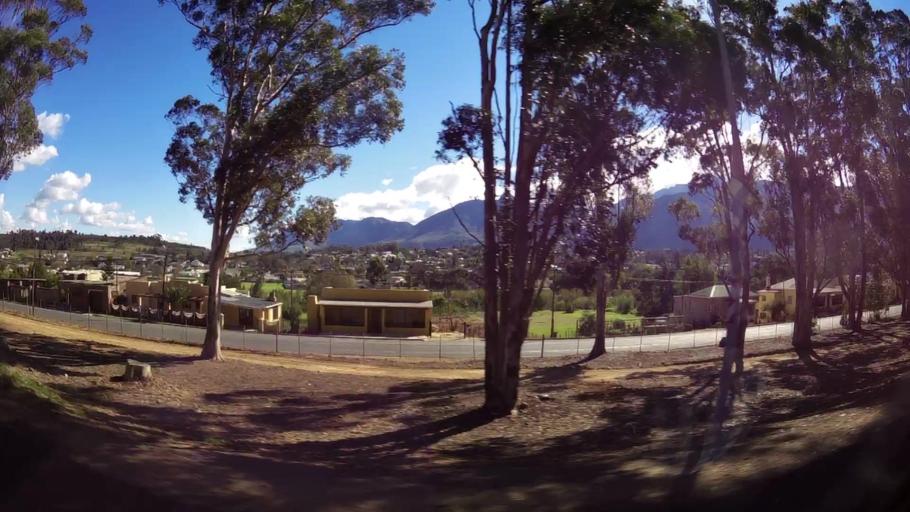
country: ZA
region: Western Cape
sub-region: Overberg District Municipality
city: Swellendam
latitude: -34.0312
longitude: 20.4394
